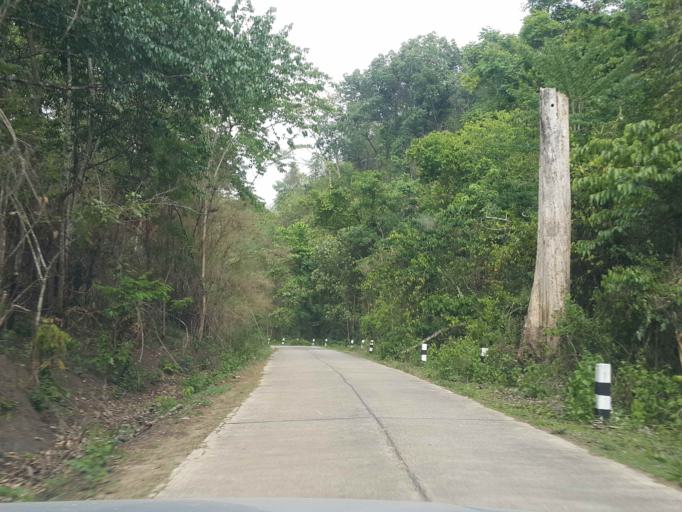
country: TH
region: Chiang Mai
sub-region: Amphoe Chiang Dao
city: Chiang Dao
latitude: 19.4115
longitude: 98.7951
